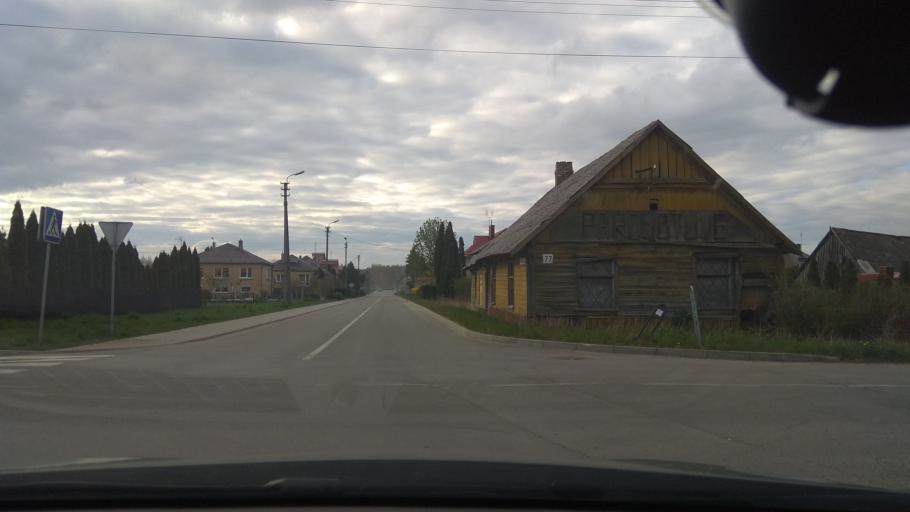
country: LT
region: Siauliu apskritis
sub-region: Joniskis
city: Joniskis
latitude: 56.2458
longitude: 23.6128
